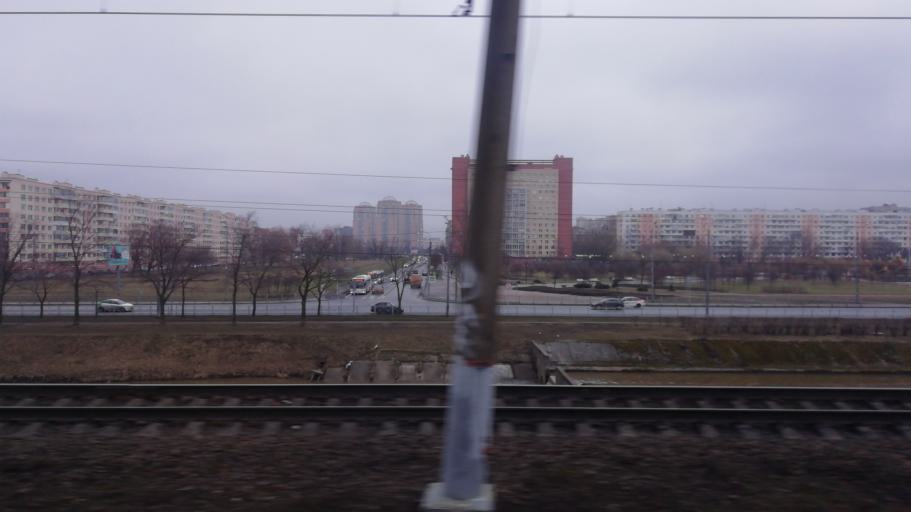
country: RU
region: St.-Petersburg
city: Kupchino
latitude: 59.8658
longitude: 30.3585
